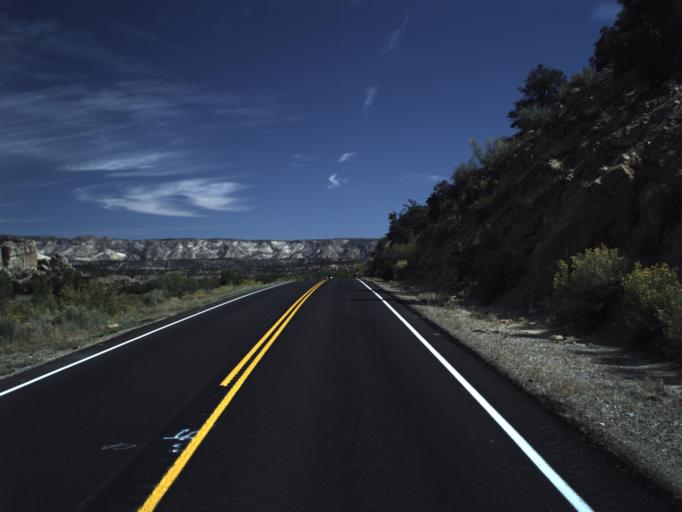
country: US
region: Utah
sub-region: Wayne County
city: Loa
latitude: 37.7630
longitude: -111.6885
